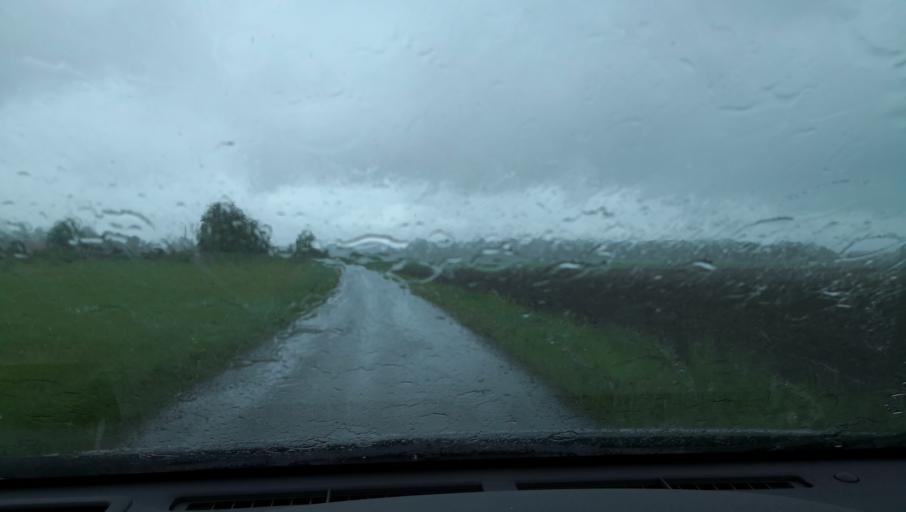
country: SE
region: Uppsala
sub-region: Enkopings Kommun
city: Orsundsbro
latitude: 59.7755
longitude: 17.3493
